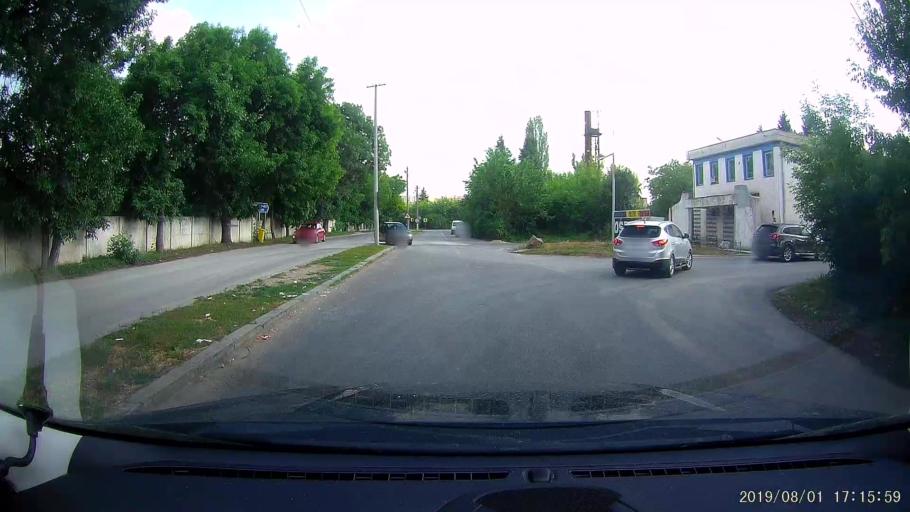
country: BG
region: Silistra
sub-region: Obshtina Silistra
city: Silistra
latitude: 44.1181
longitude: 27.2770
